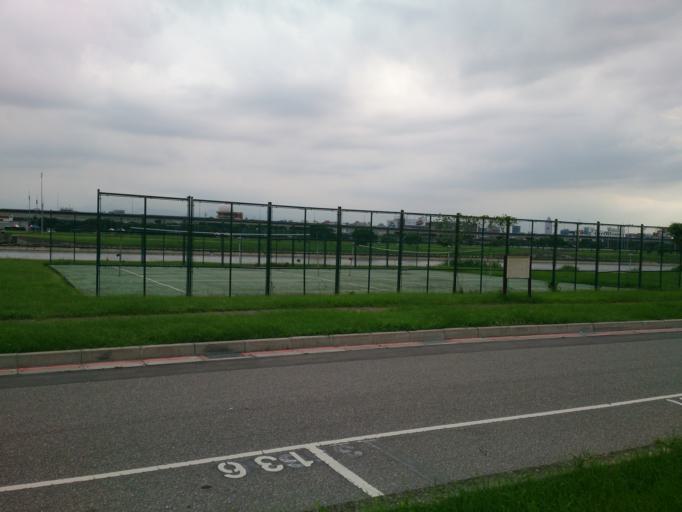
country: TW
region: Taipei
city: Taipei
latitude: 25.0771
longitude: 121.5523
